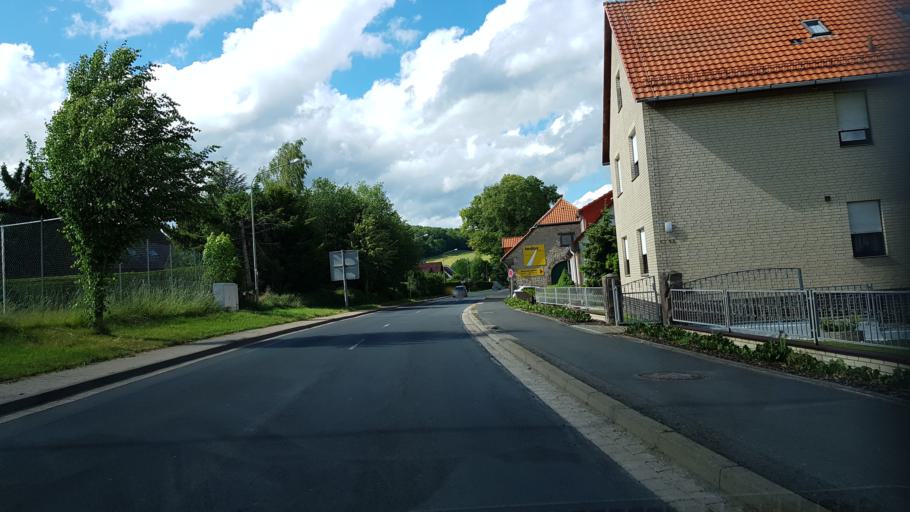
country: DE
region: Lower Saxony
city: Hardegsen
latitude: 51.5992
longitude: 9.8539
